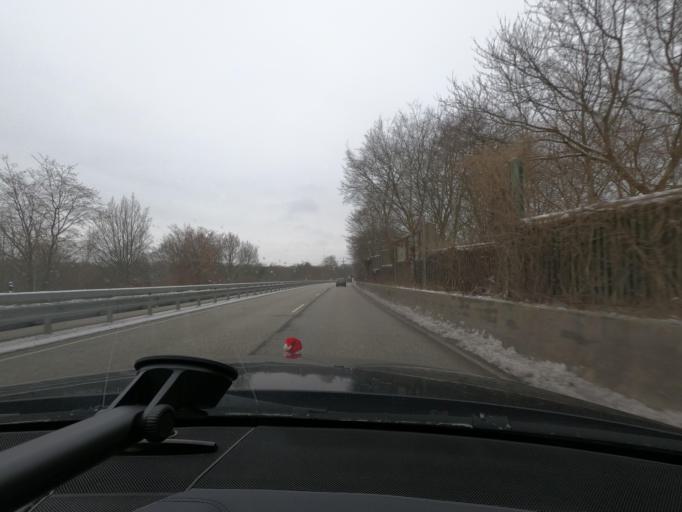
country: DE
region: Schleswig-Holstein
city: Harrislee
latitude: 54.7857
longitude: 9.4044
